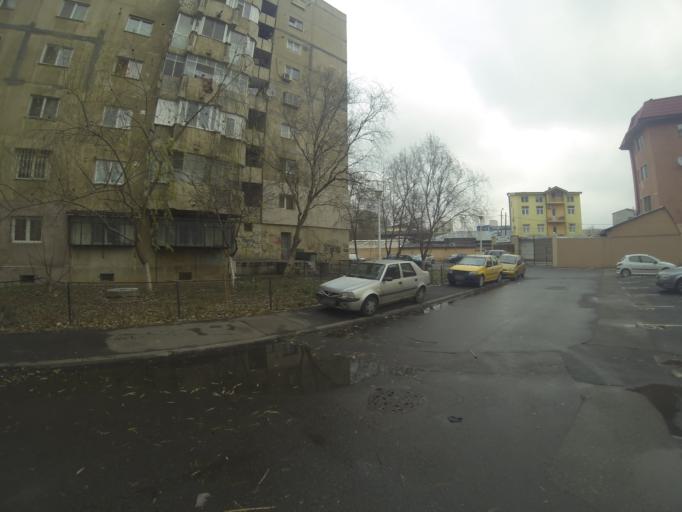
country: RO
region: Bucuresti
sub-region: Municipiul Bucuresti
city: Bucuresti
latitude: 44.4096
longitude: 26.0776
